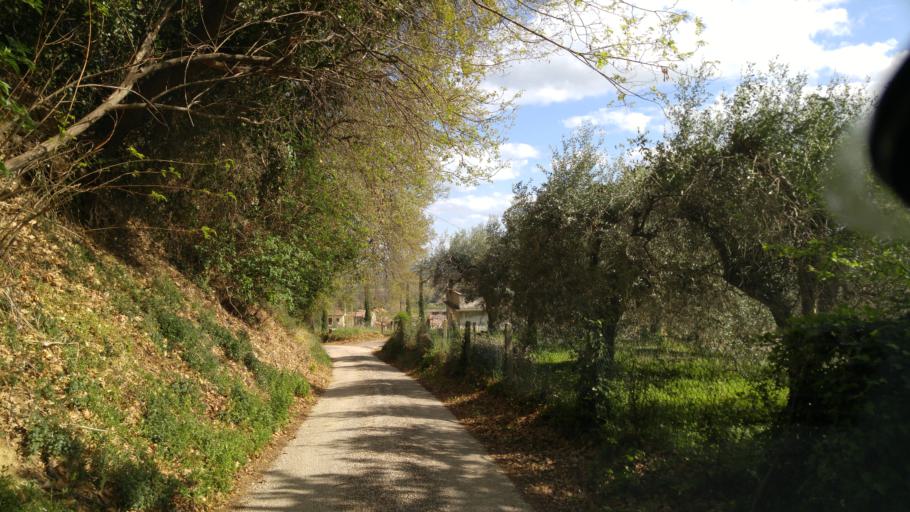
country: IT
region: The Marches
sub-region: Provincia di Pesaro e Urbino
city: Fenile
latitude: 43.8447
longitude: 12.9635
